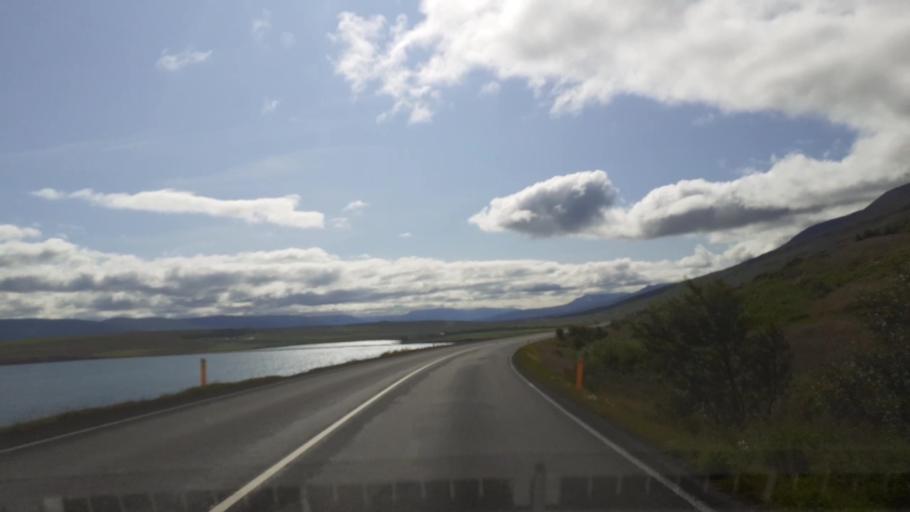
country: IS
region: Northeast
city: Akureyri
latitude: 65.8794
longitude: -18.2657
